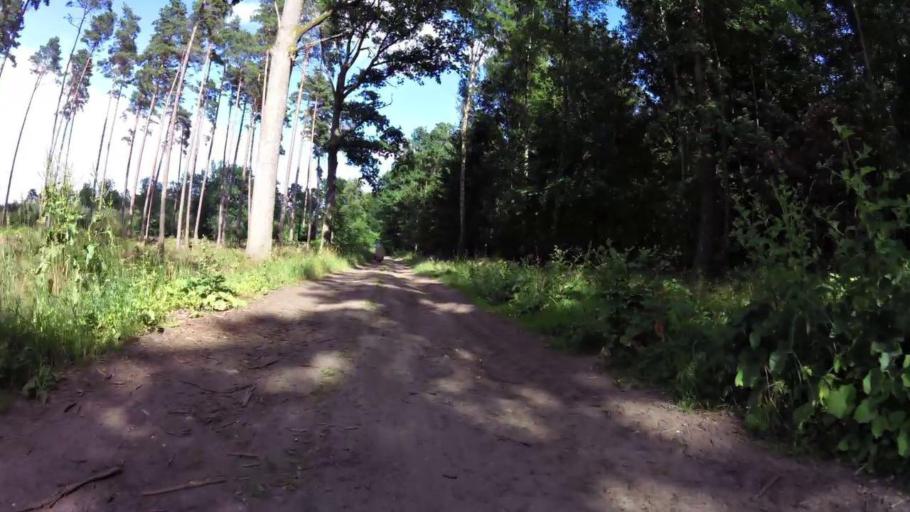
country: PL
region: West Pomeranian Voivodeship
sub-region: Powiat lobeski
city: Lobez
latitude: 53.6731
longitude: 15.7131
